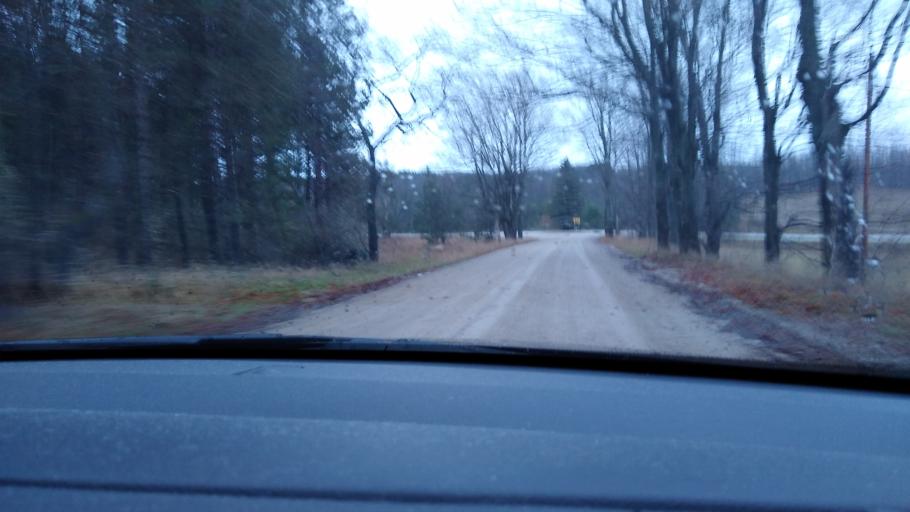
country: US
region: Michigan
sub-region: Wexford County
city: Cadillac
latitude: 44.1663
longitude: -85.3952
